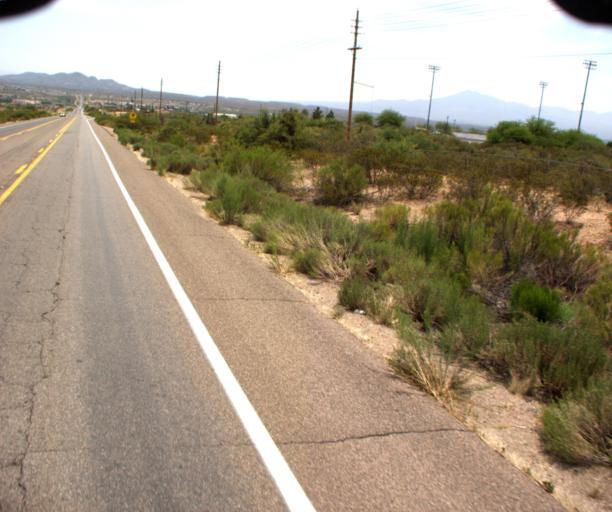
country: US
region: Arizona
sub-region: Gila County
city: Peridot
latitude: 33.3027
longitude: -110.4753
